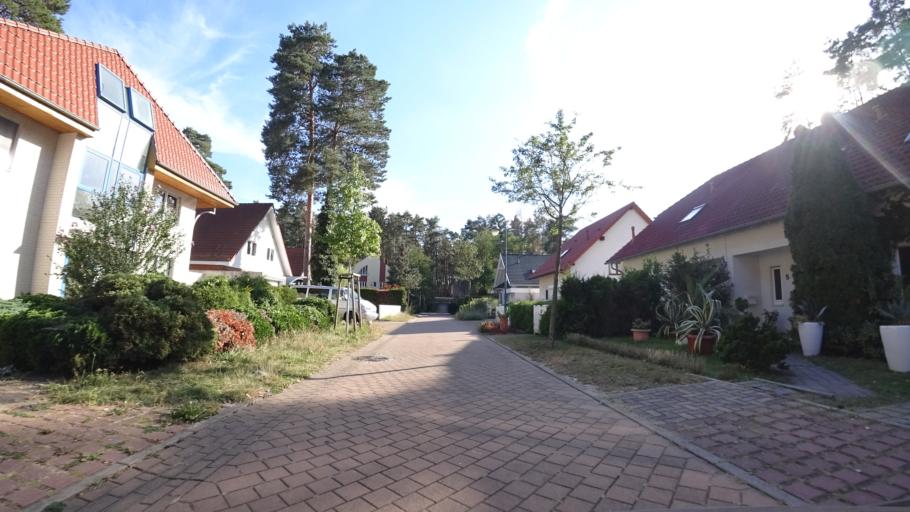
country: DE
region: Brandenburg
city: Stahnsdorf
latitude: 52.3996
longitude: 13.1982
